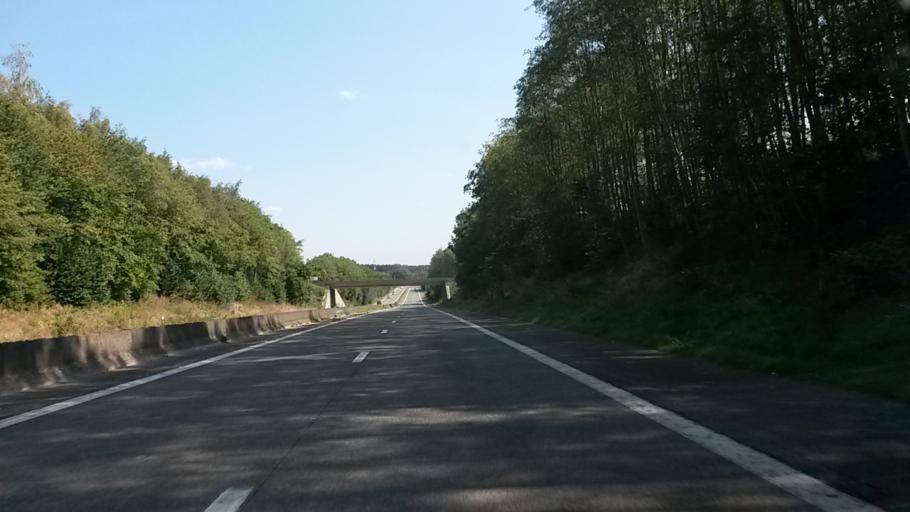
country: BE
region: Wallonia
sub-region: Province du Hainaut
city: Anderlues
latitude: 50.4024
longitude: 4.3261
